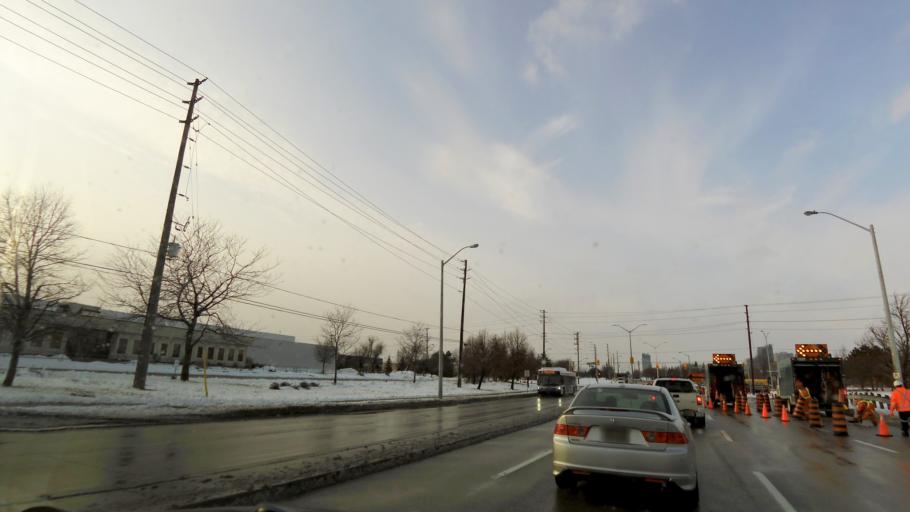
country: CA
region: Ontario
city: Brampton
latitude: 43.6986
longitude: -79.7169
